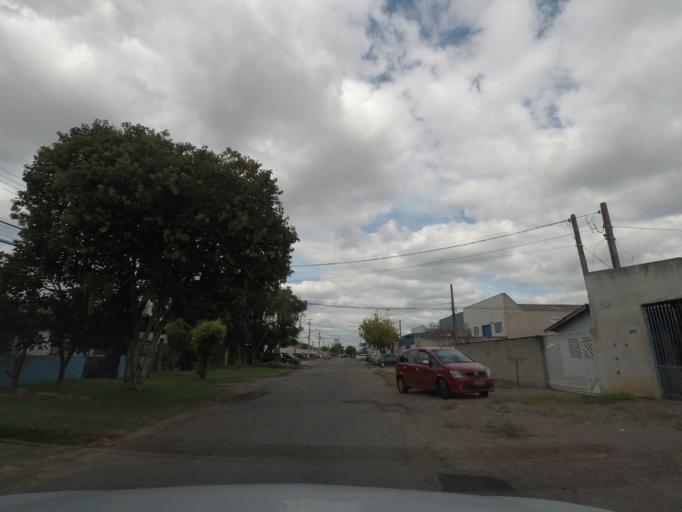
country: BR
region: Parana
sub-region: Sao Jose Dos Pinhais
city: Sao Jose dos Pinhais
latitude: -25.4850
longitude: -49.2401
